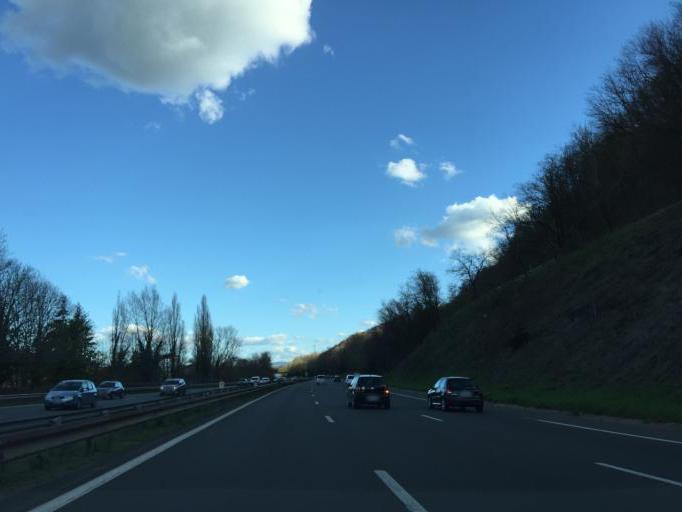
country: FR
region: Rhone-Alpes
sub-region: Departement de la Loire
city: La Fouillouse
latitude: 45.5004
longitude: 4.3109
